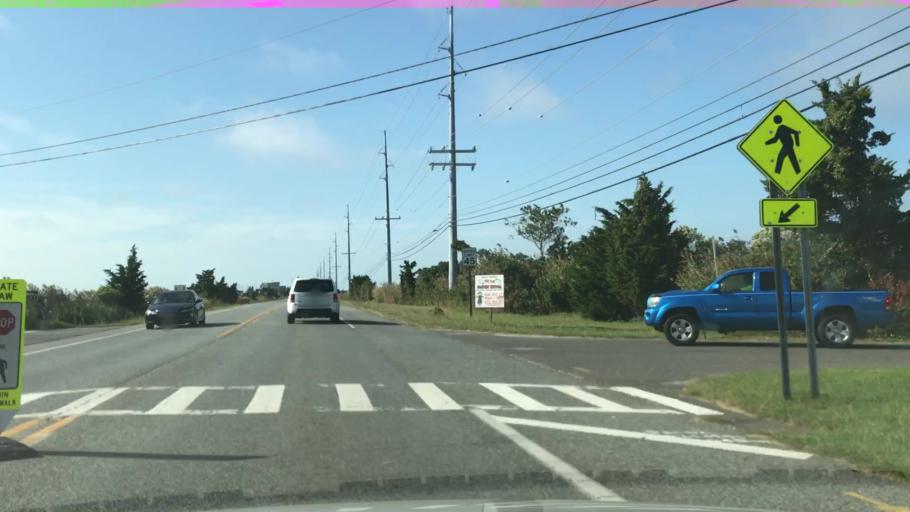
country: US
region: New Jersey
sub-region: Cape May County
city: Cape May Court House
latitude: 39.0611
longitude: -74.7724
